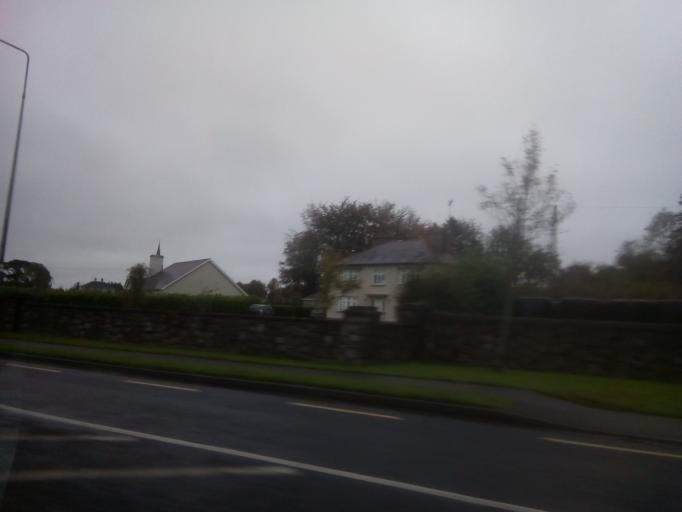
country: IE
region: Leinster
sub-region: An Longfort
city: Edgeworthstown
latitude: 53.6913
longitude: -7.6068
